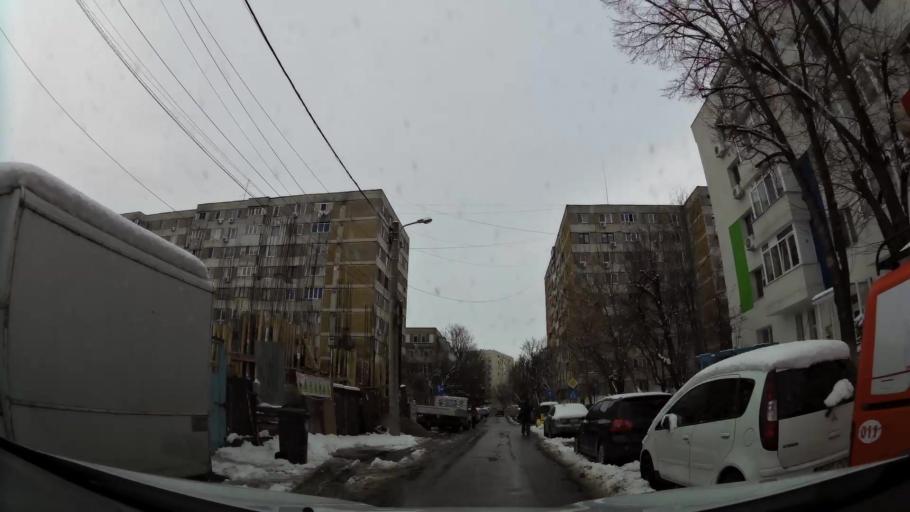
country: RO
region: Ilfov
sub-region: Comuna Popesti-Leordeni
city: Popesti-Leordeni
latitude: 44.3856
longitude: 26.1331
